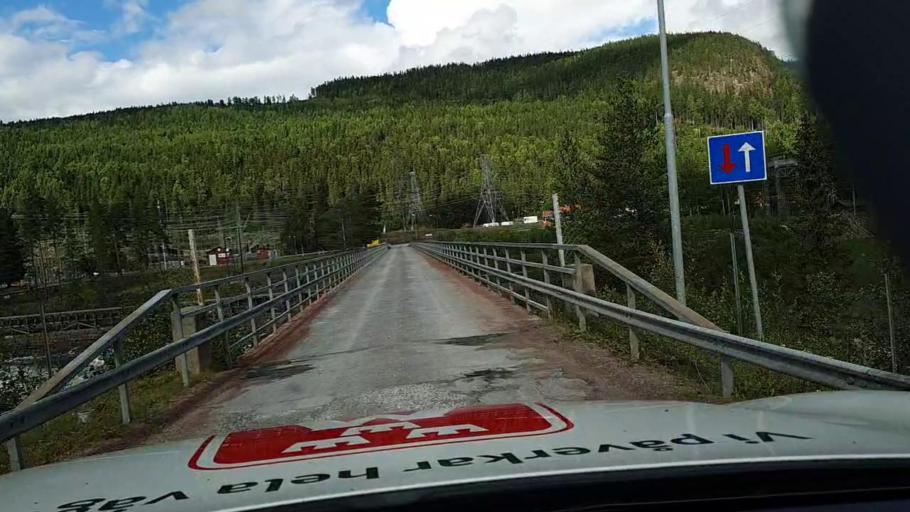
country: SE
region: Jaemtland
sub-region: Ragunda Kommun
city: Hammarstrand
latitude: 63.1451
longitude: 16.0741
